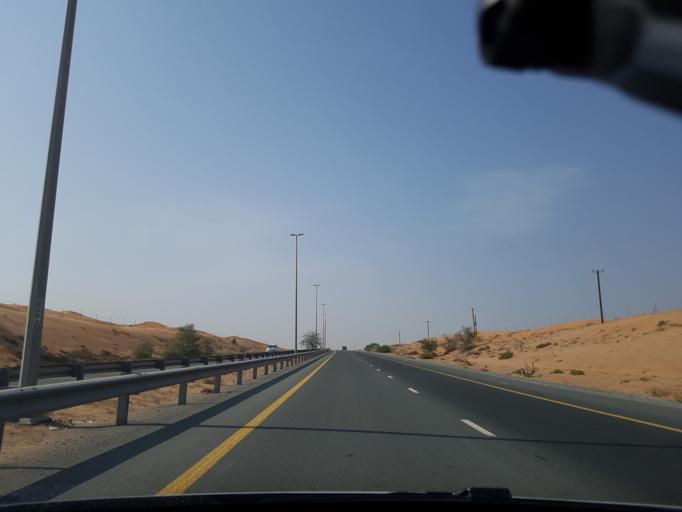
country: AE
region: Umm al Qaywayn
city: Umm al Qaywayn
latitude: 25.5173
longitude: 55.7431
